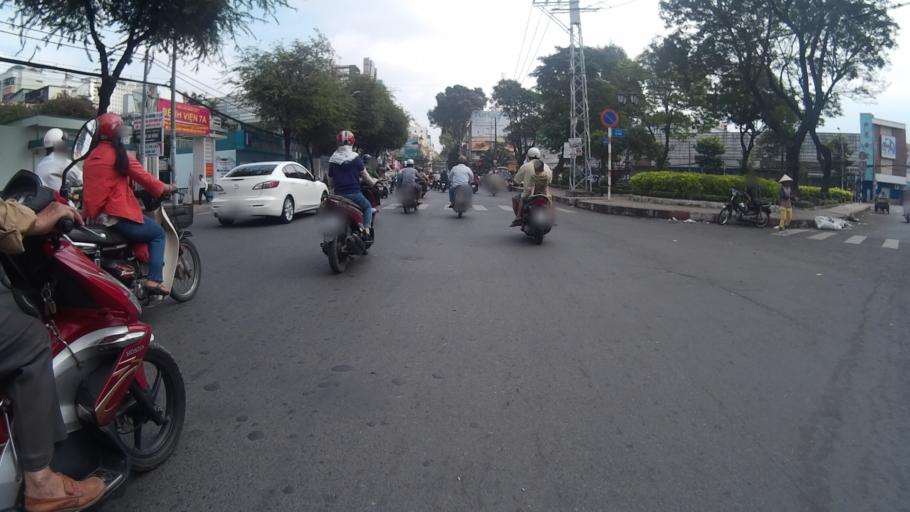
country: VN
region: Ho Chi Minh City
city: Quan Nam
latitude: 10.7549
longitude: 106.6707
